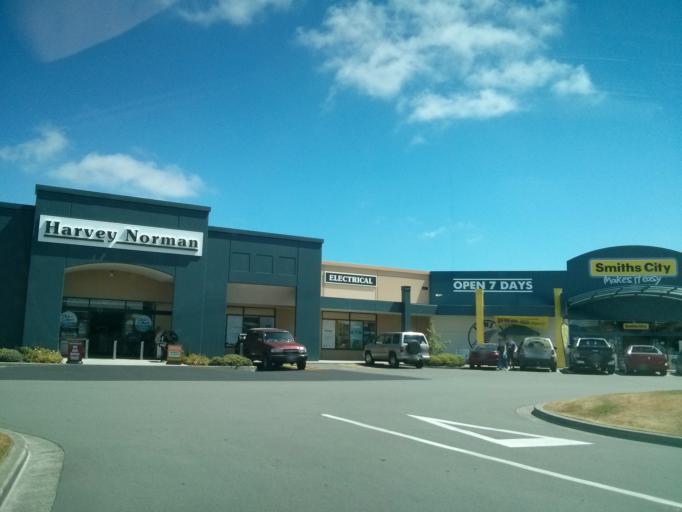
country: NZ
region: Canterbury
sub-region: Christchurch City
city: Christchurch
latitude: -43.4598
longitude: 172.6244
